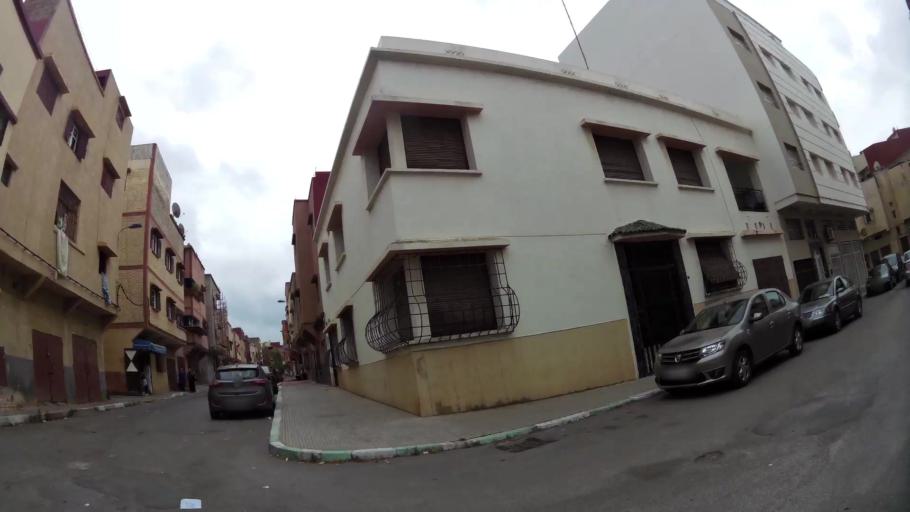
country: MA
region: Rabat-Sale-Zemmour-Zaer
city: Sale
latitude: 34.0411
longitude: -6.8059
